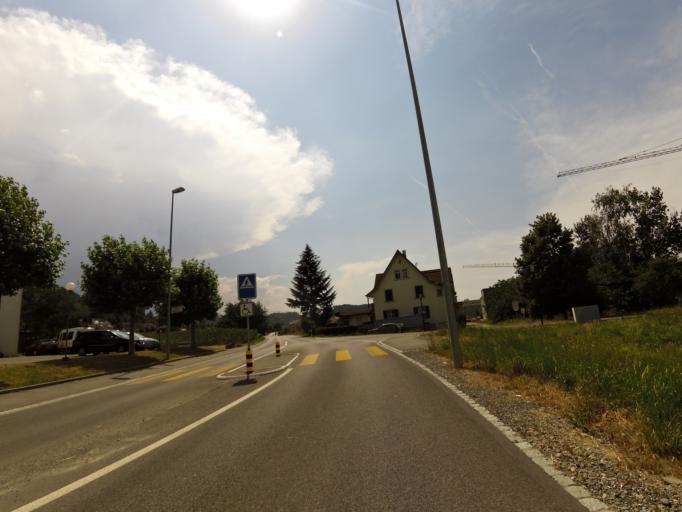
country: CH
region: Aargau
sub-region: Bezirk Lenzburg
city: Staufen
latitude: 47.3860
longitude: 8.1631
